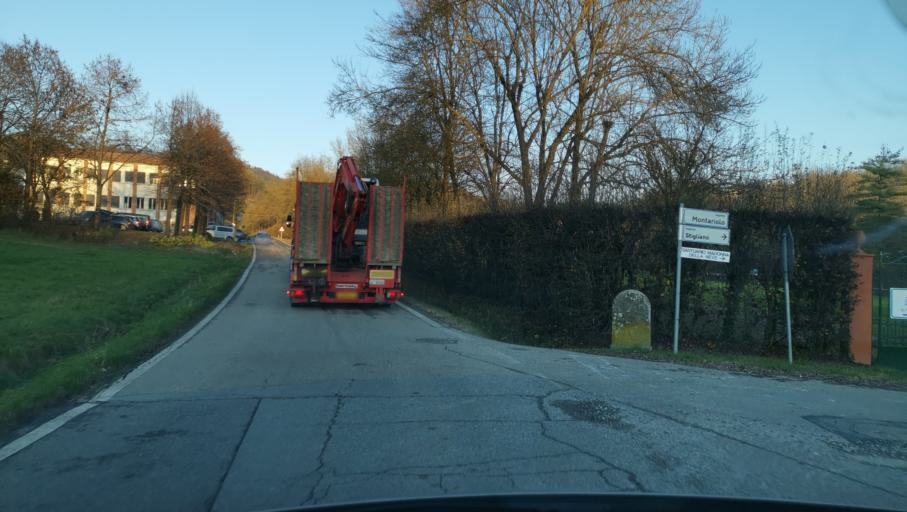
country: IT
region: Piedmont
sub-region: Provincia di Torino
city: Rivalba
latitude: 45.1089
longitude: 7.8949
